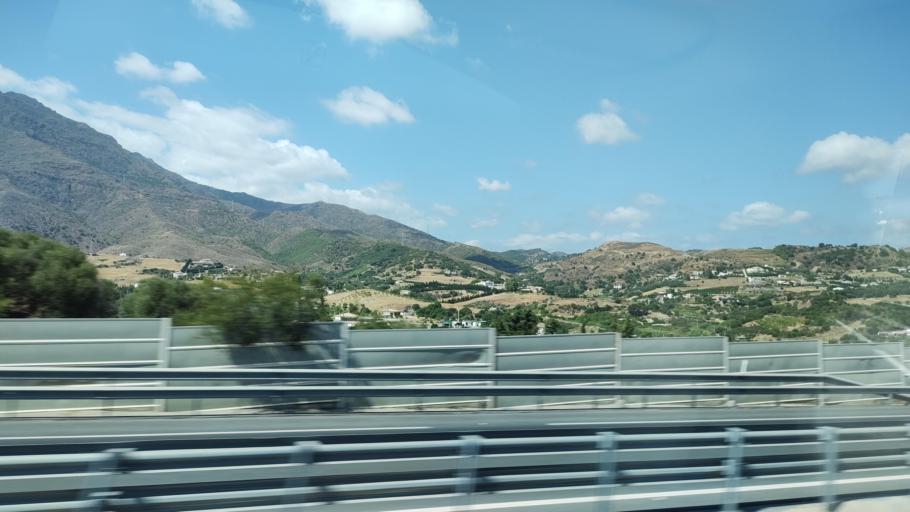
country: ES
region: Andalusia
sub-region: Provincia de Malaga
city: Estepona
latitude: 36.4327
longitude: -5.1876
